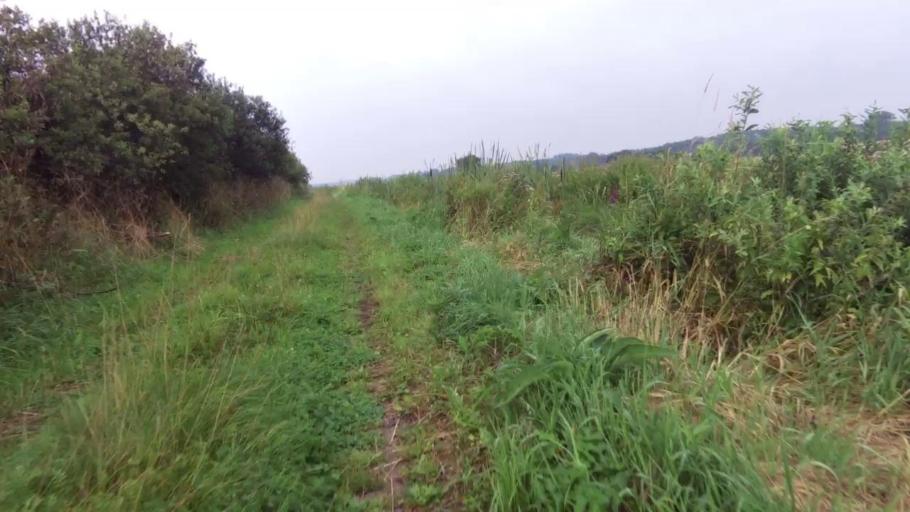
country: PL
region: West Pomeranian Voivodeship
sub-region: Powiat choszczenski
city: Choszczno
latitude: 53.2452
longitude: 15.4318
